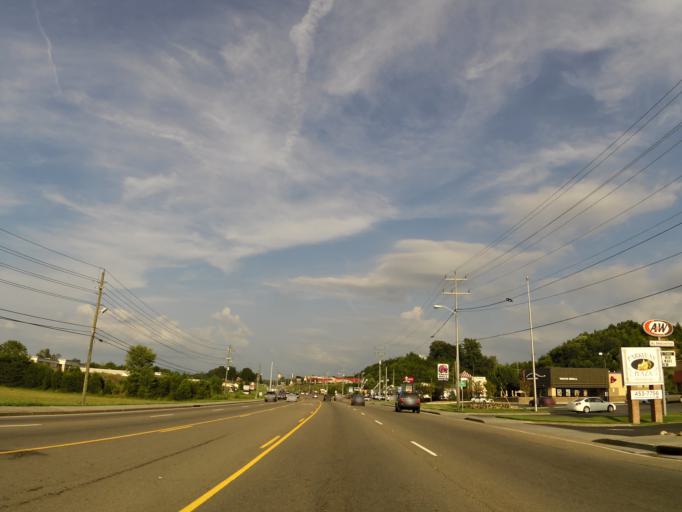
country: US
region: Tennessee
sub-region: Sevier County
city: Sevierville
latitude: 35.8643
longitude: -83.5453
